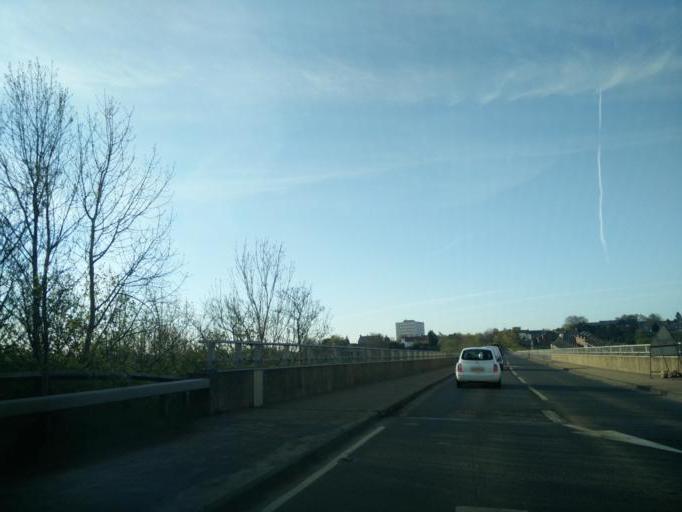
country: GB
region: England
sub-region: County Durham
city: Bishop Auckland
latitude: 54.6684
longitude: -1.6826
